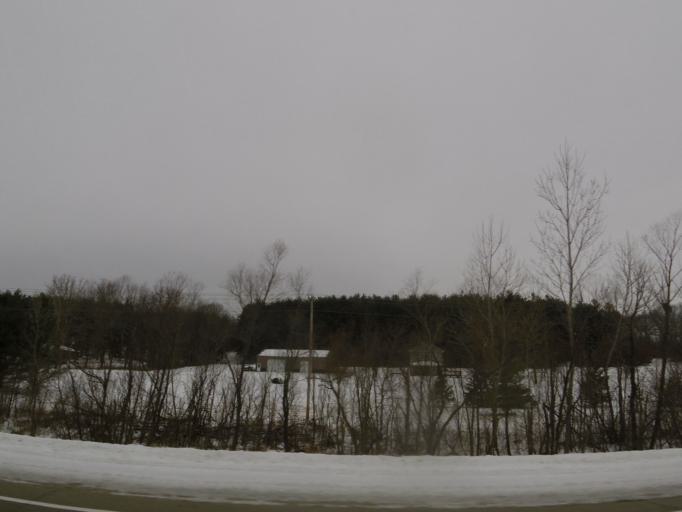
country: US
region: Illinois
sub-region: Hancock County
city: Nauvoo
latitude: 40.5638
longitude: -91.5655
